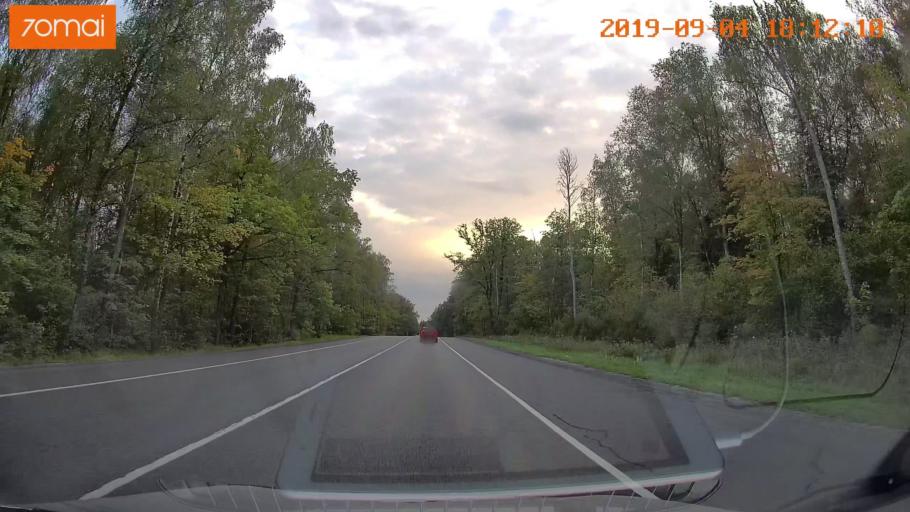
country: RU
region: Moskovskaya
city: Lopatinskiy
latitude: 55.3723
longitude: 38.7460
